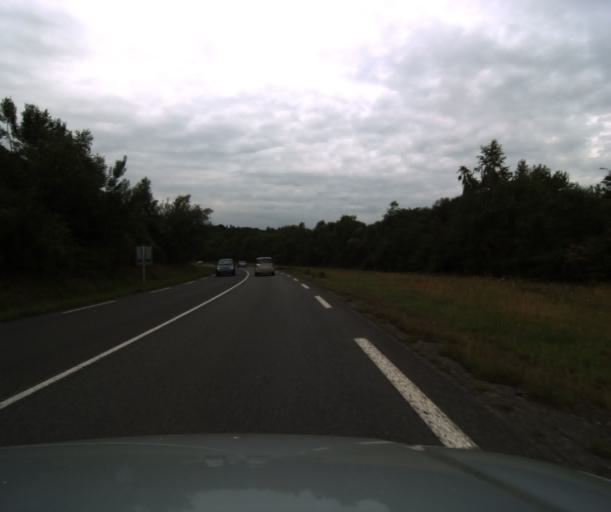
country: FR
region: Midi-Pyrenees
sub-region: Departement des Hautes-Pyrenees
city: Juillan
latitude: 43.1881
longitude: 0.0091
